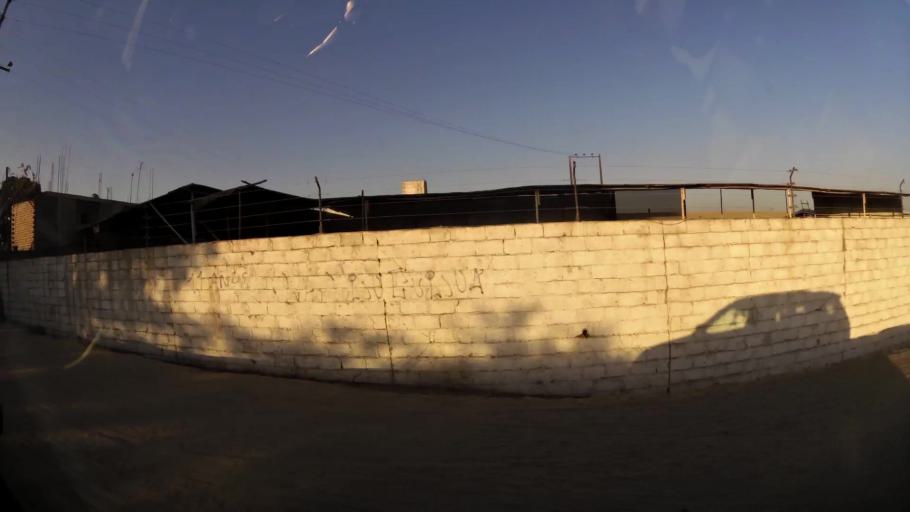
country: PE
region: Ica
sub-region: Provincia de Ica
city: Ica
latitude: -14.0743
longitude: -75.7192
